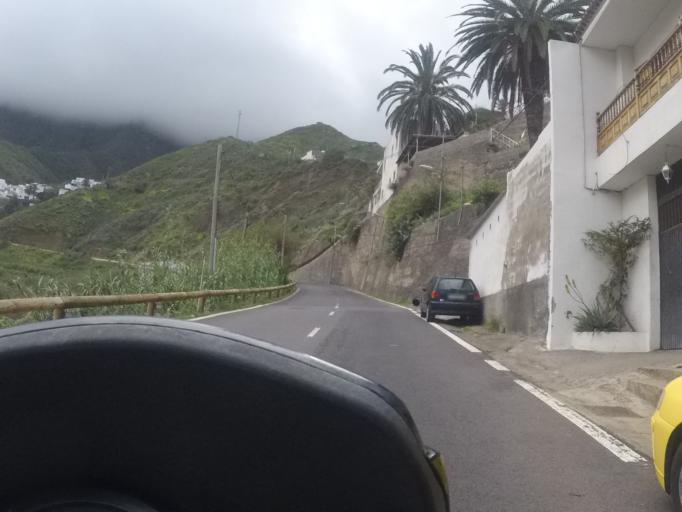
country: ES
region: Canary Islands
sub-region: Provincia de Santa Cruz de Tenerife
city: Santa Cruz de Tenerife
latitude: 28.5607
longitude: -16.2166
